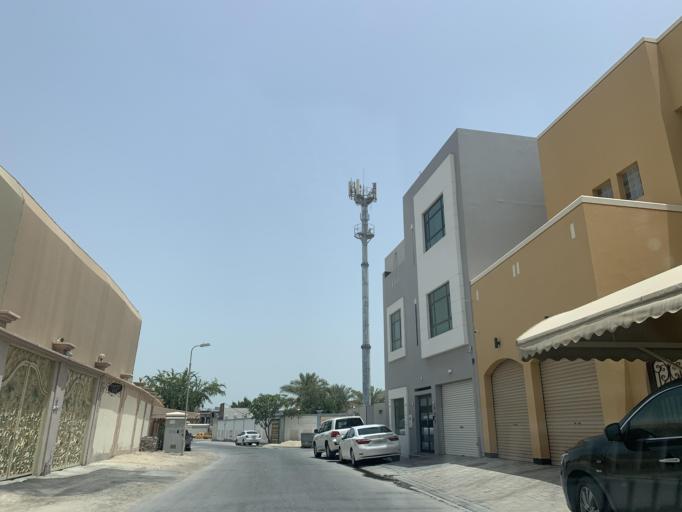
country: BH
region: Northern
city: Sitrah
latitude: 26.1451
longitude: 50.5888
